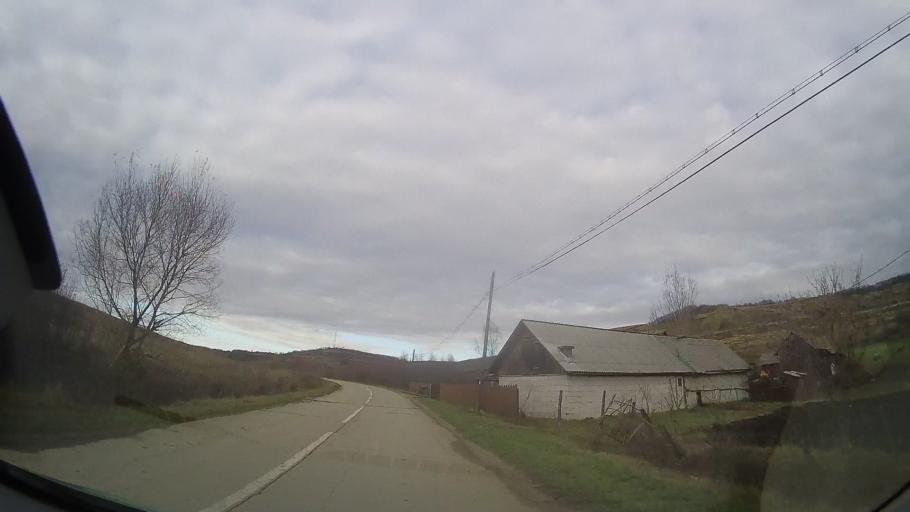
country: RO
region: Bistrita-Nasaud
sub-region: Comuna Micestii de Campie
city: Micestii de Campie
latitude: 46.8389
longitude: 24.3043
